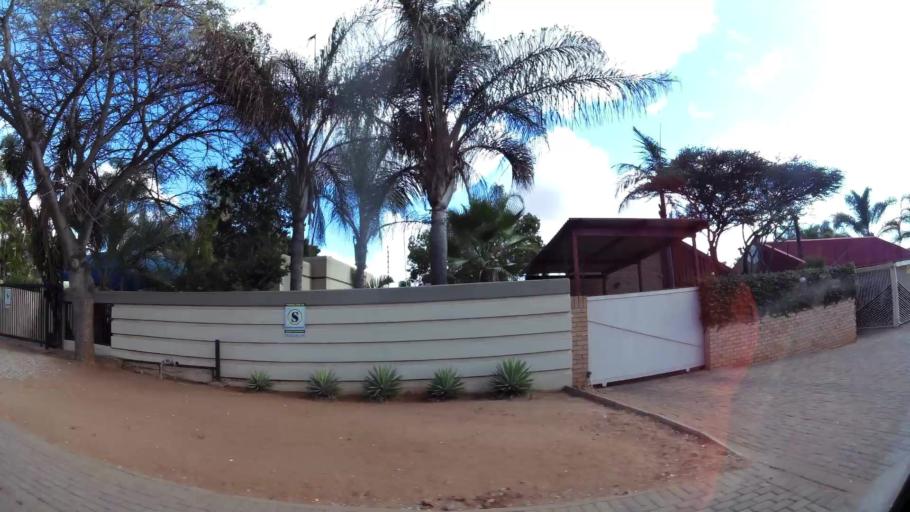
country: ZA
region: Limpopo
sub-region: Capricorn District Municipality
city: Polokwane
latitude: -23.8964
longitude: 29.4749
